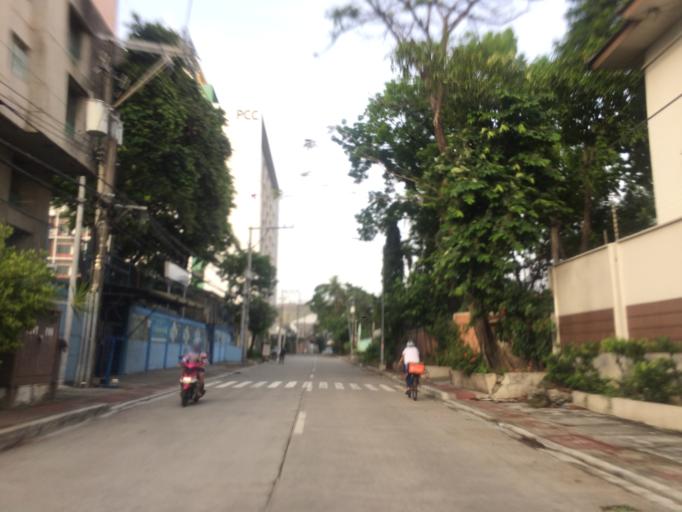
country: PH
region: Calabarzon
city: Del Monte
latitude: 14.6233
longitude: 121.0044
